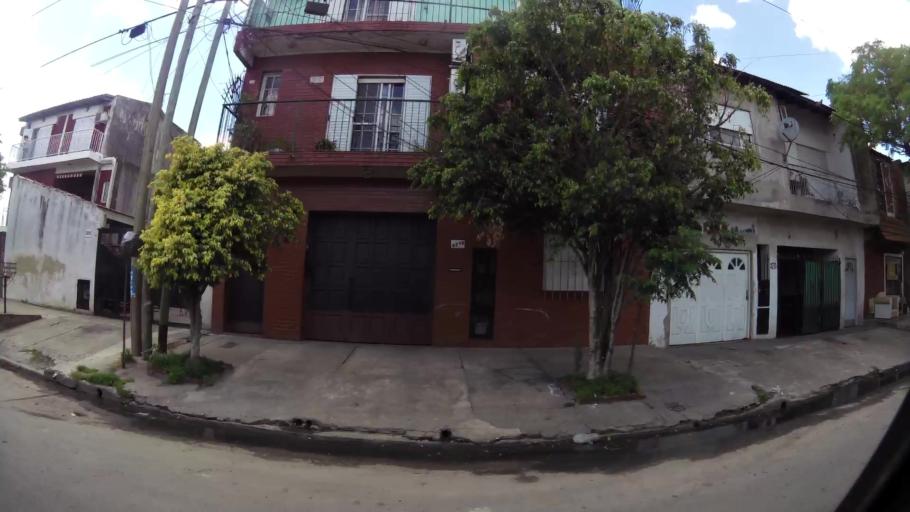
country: AR
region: Buenos Aires
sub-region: Partido de Lanus
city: Lanus
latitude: -34.7122
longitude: -58.4290
